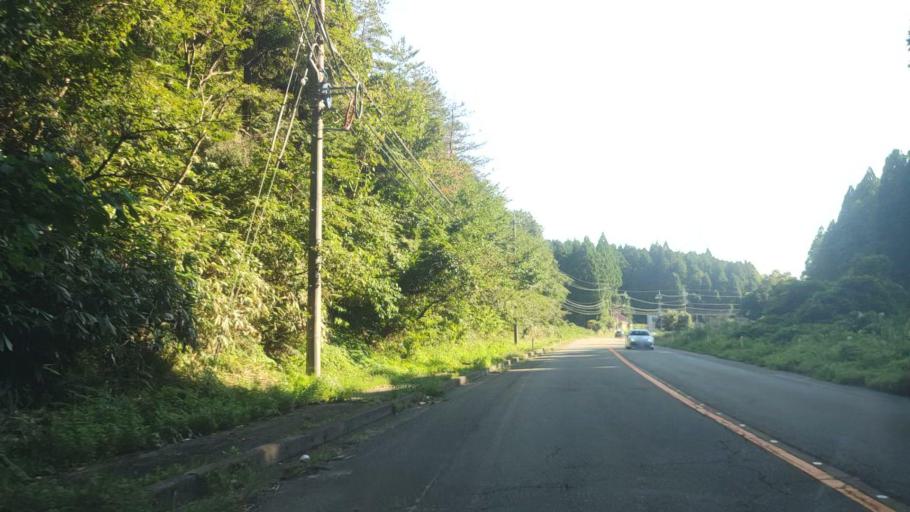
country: JP
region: Ishikawa
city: Nanao
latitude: 37.1253
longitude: 136.8634
